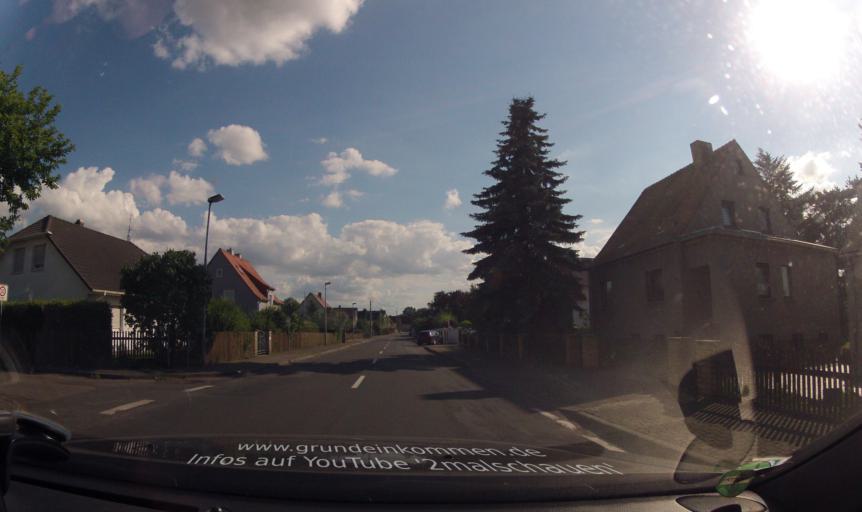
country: DE
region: Saxony
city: Falkenhain
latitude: 51.4021
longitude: 12.8718
